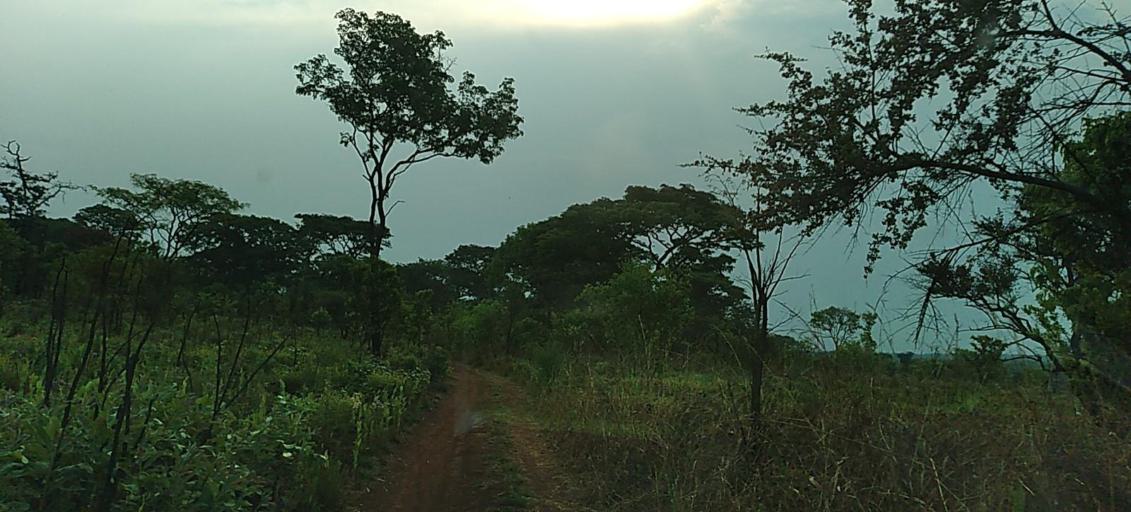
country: ZM
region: North-Western
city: Solwezi
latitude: -12.0439
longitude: 26.0246
